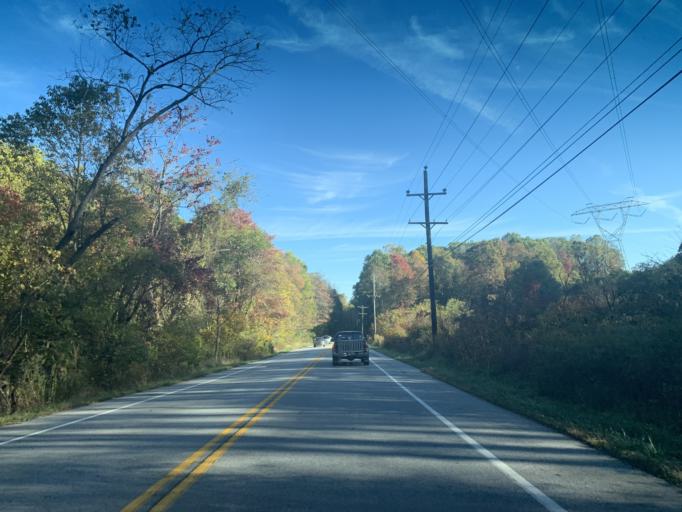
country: US
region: Pennsylvania
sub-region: Chester County
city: Parkesburg
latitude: 39.9468
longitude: -75.9147
